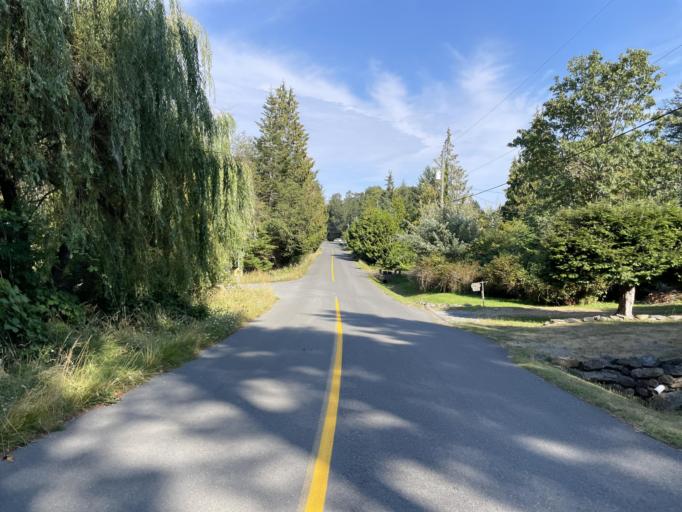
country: CA
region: British Columbia
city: Nanaimo
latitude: 49.1711
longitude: -123.7807
